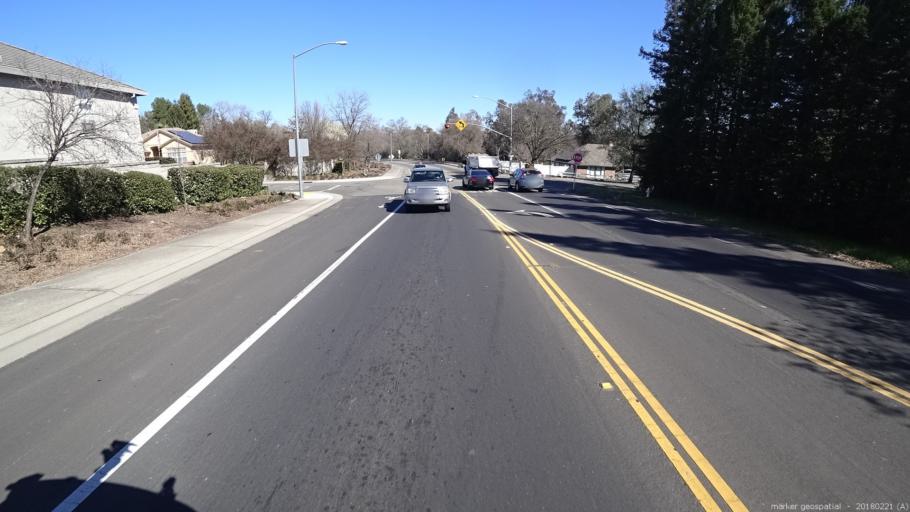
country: US
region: California
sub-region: Sacramento County
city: Citrus Heights
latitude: 38.7171
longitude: -121.2437
